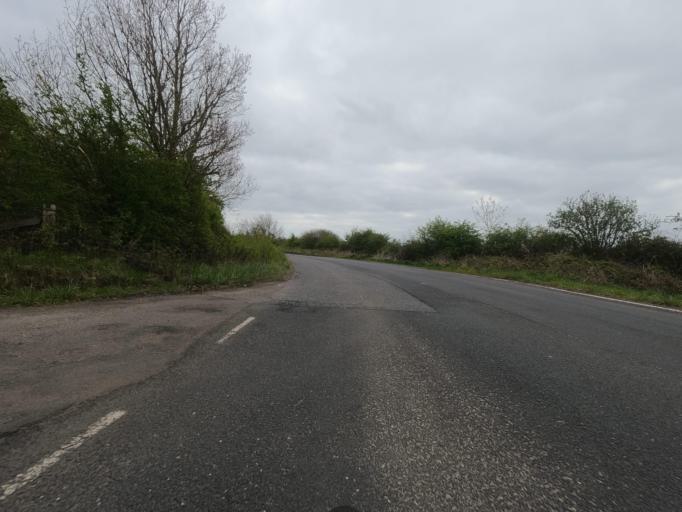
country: GB
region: England
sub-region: Newcastle upon Tyne
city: Dinnington
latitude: 55.0641
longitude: -1.6846
